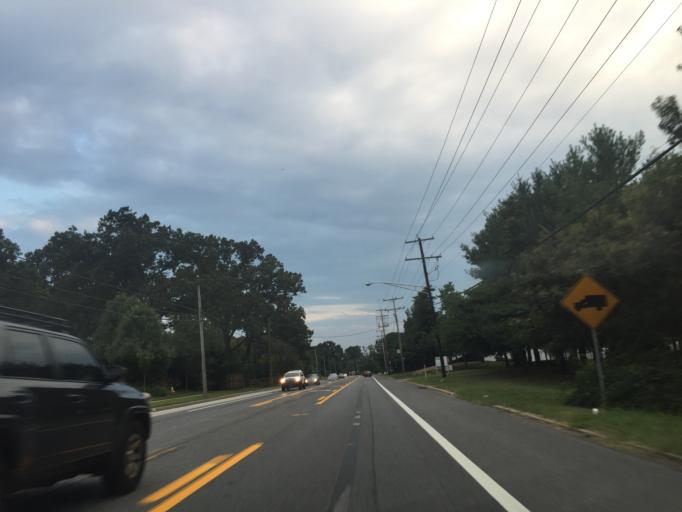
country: US
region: Maryland
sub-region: Anne Arundel County
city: Severn
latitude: 39.1221
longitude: -76.6900
